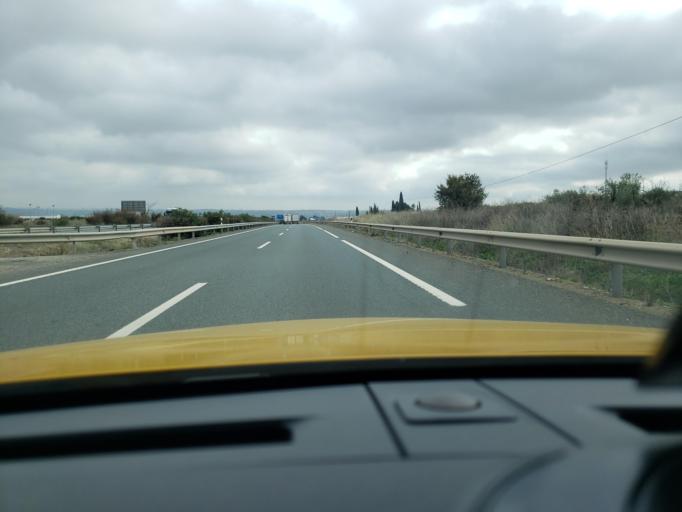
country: ES
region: Andalusia
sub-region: Provincia de Sevilla
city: Carrion de los Cespedes
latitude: 37.3608
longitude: -6.2817
